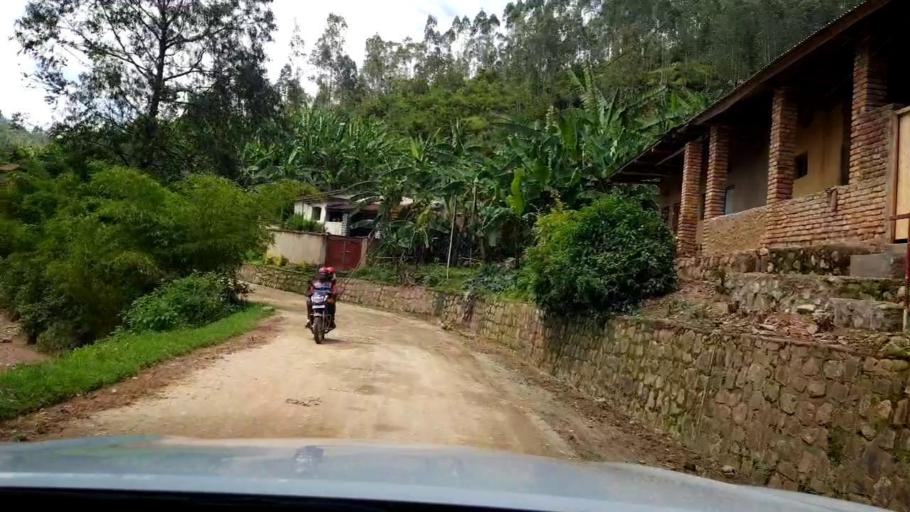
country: RW
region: Southern Province
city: Gitarama
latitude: -1.9245
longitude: 29.6536
